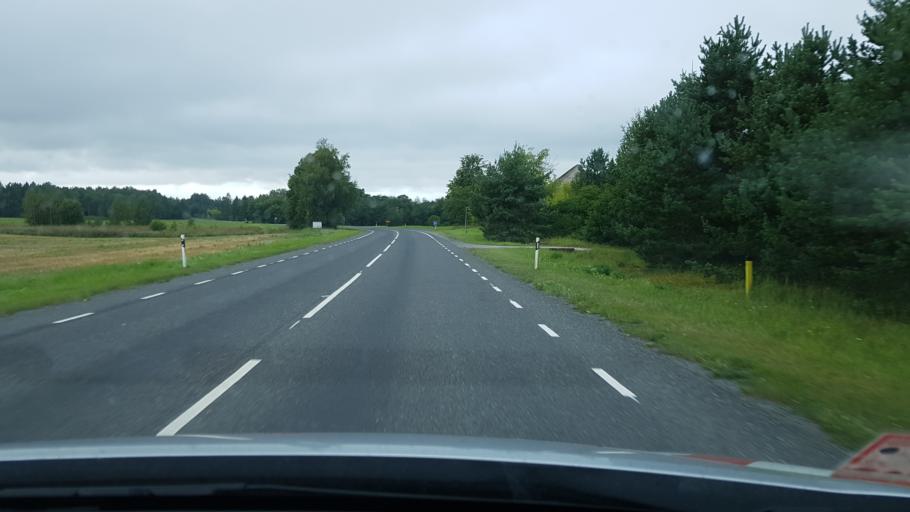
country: EE
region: Vorumaa
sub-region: Antsla vald
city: Vana-Antsla
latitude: 57.9439
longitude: 26.3810
